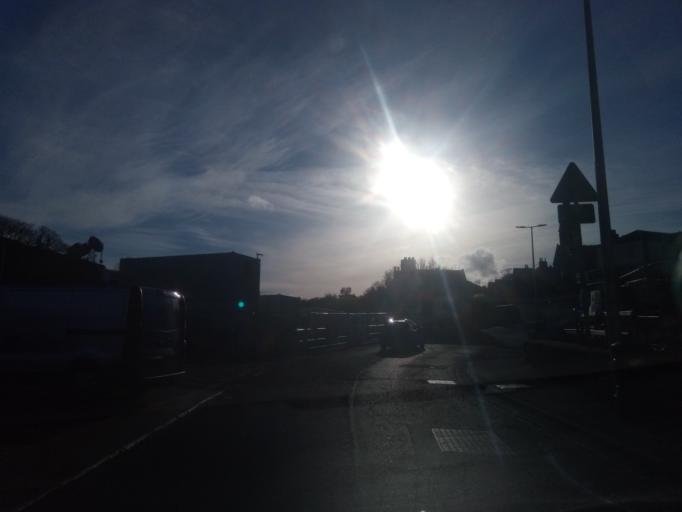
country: GB
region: Scotland
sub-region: The Scottish Borders
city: Eyemouth
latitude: 55.8703
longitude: -2.0892
